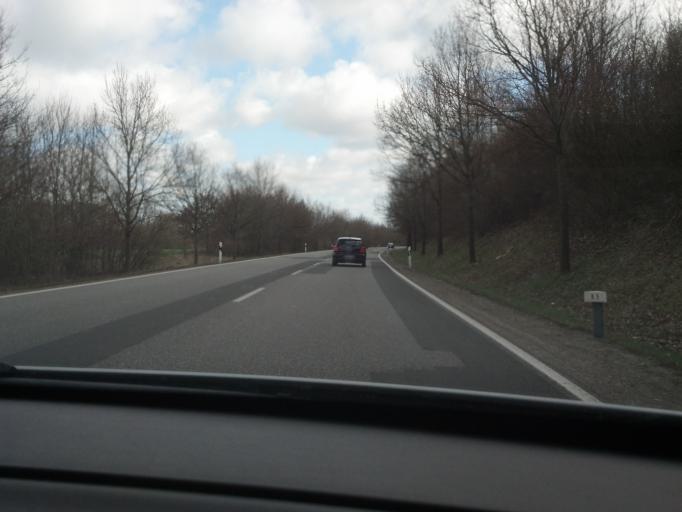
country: DE
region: Mecklenburg-Vorpommern
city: Boizenburg
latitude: 53.3852
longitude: 10.7068
